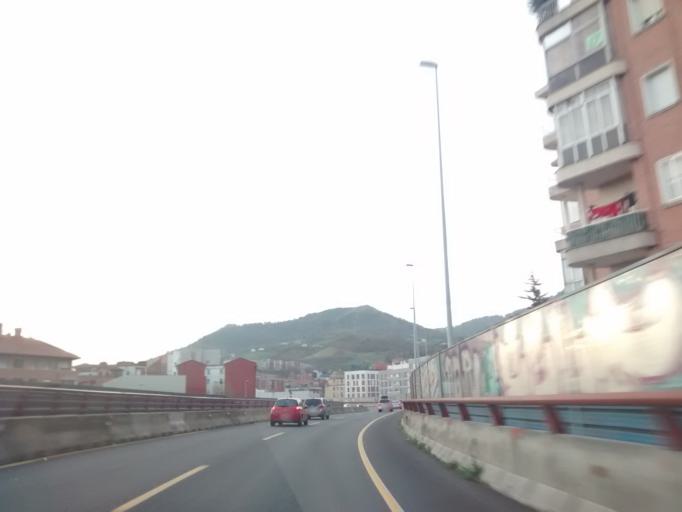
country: ES
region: Basque Country
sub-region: Bizkaia
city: Bilbao
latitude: 43.2549
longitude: -2.9495
